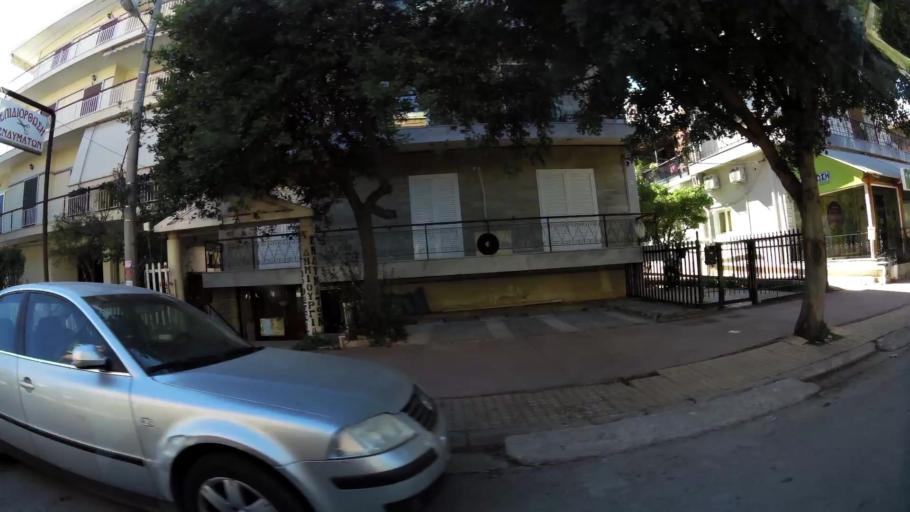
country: GR
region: Attica
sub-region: Nomarchia Athinas
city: Vrilissia
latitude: 38.0258
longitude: 23.8227
